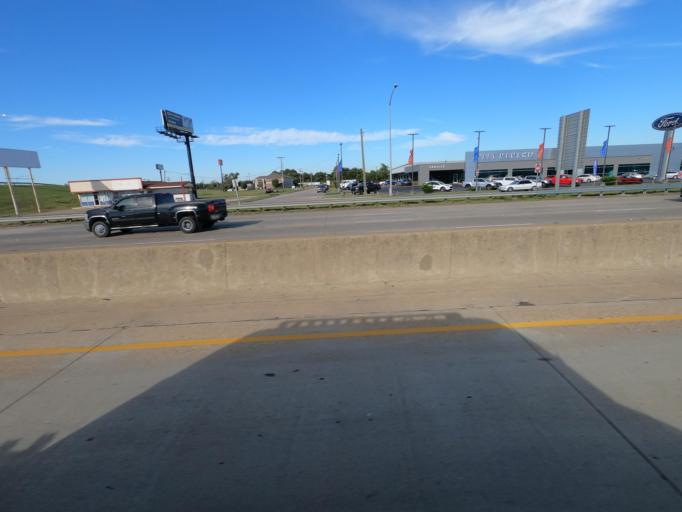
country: US
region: Arkansas
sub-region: Crittenden County
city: West Memphis
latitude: 35.1566
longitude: -90.1556
